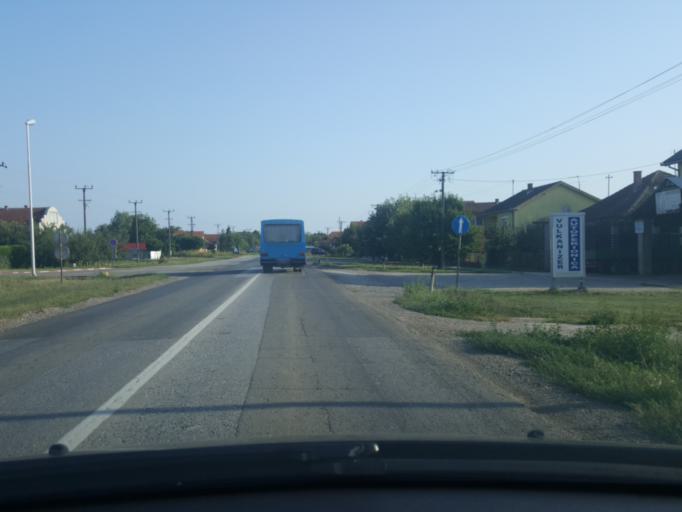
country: RS
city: Hrtkovci
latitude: 44.8908
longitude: 19.7639
